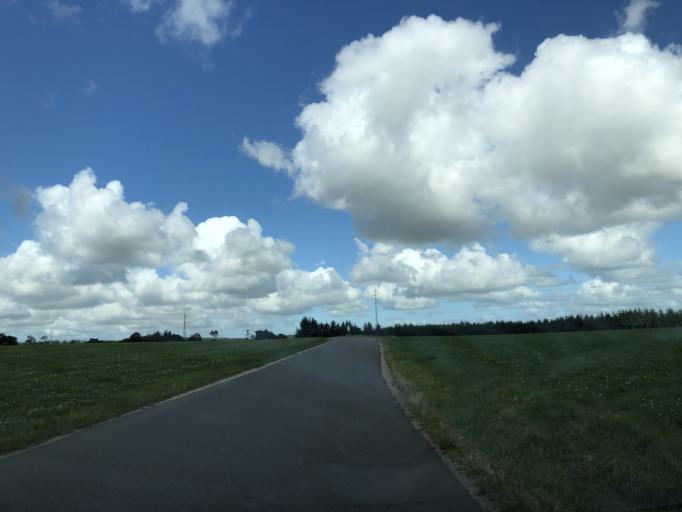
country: DK
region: Central Jutland
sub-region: Struer Kommune
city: Struer
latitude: 56.4776
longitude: 8.5330
